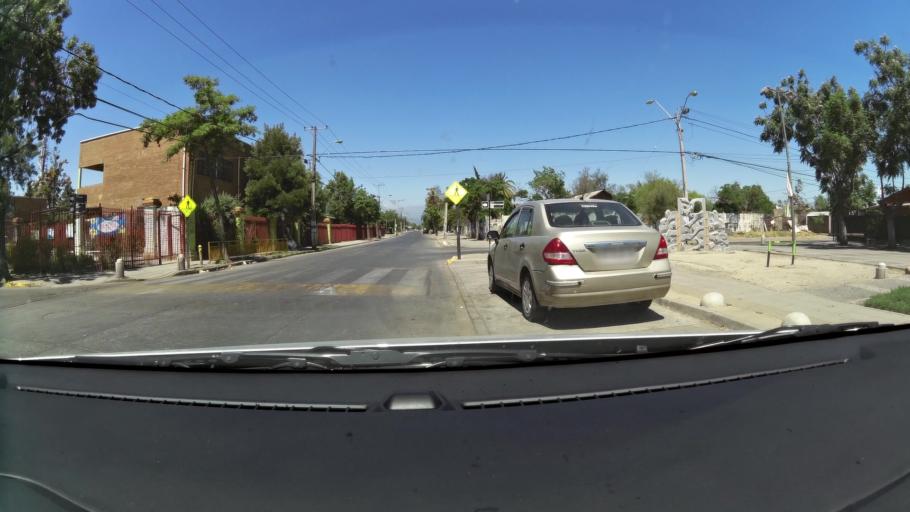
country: CL
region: Santiago Metropolitan
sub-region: Provincia de Maipo
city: San Bernardo
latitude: -33.5717
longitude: -70.6815
